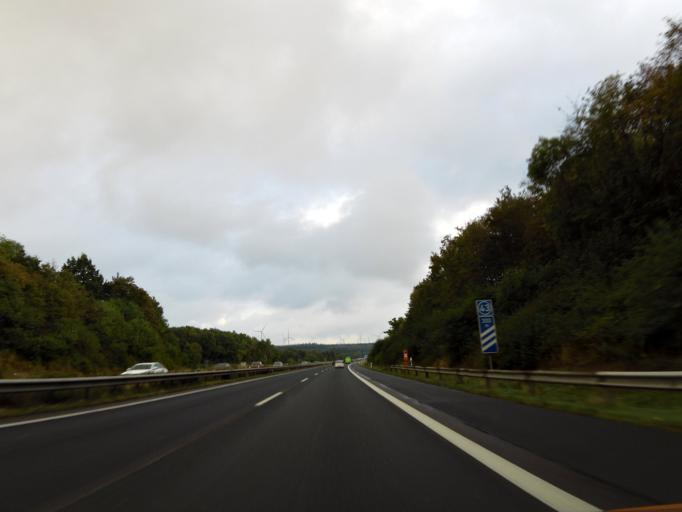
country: DE
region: Rheinland-Pfalz
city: Hungenroth
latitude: 50.1210
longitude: 7.6003
